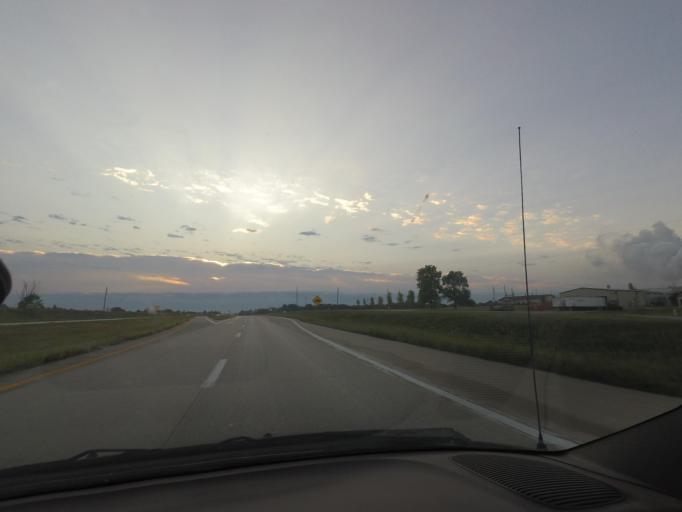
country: US
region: Missouri
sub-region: Macon County
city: Macon
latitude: 39.7509
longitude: -92.3859
